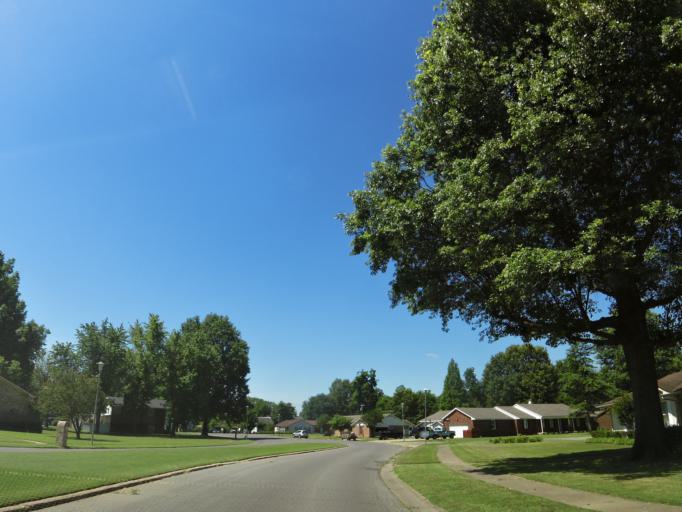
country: US
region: Missouri
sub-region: New Madrid County
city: New Madrid
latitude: 36.5971
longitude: -89.5267
